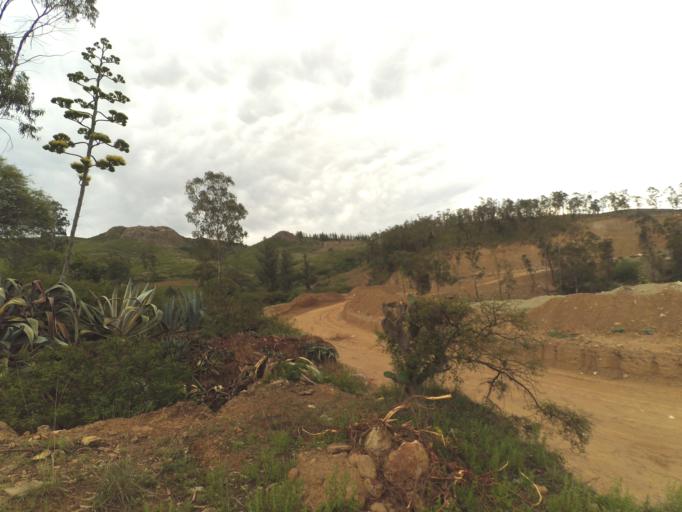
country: BO
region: Chuquisaca
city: Padilla
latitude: -19.3137
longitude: -64.3088
